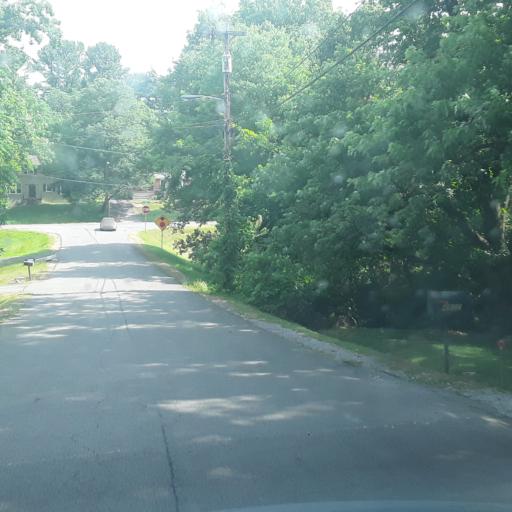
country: US
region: Tennessee
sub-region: Davidson County
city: Oak Hill
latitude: 36.0733
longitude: -86.7394
